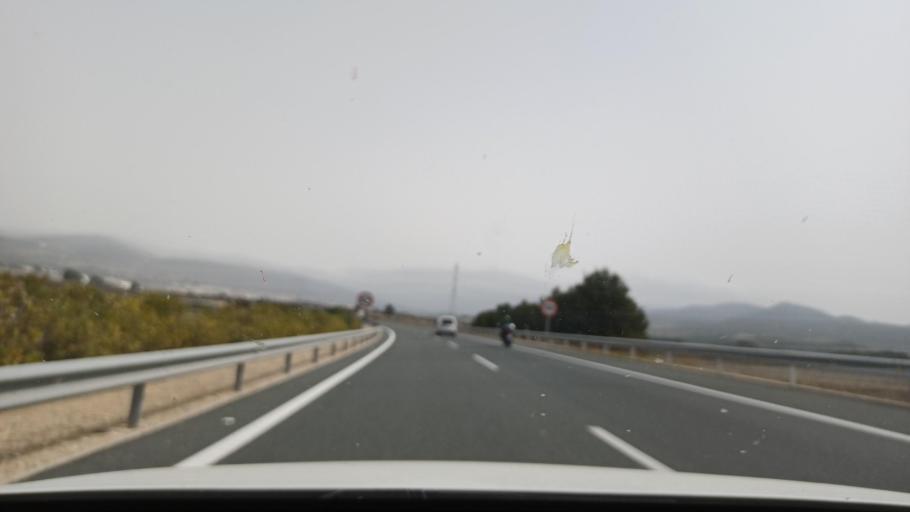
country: ES
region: Valencia
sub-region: Provincia de Alicante
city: Ibi
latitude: 38.5939
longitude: -0.6150
